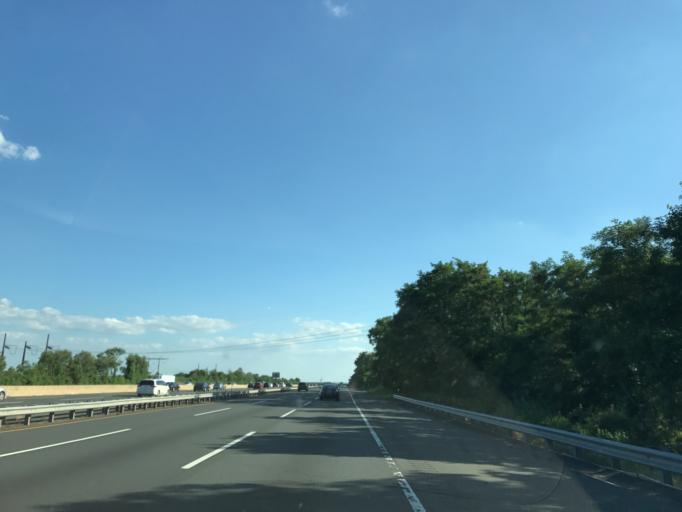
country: US
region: New Jersey
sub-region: Middlesex County
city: Helmetta
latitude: 40.3901
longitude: -74.4574
